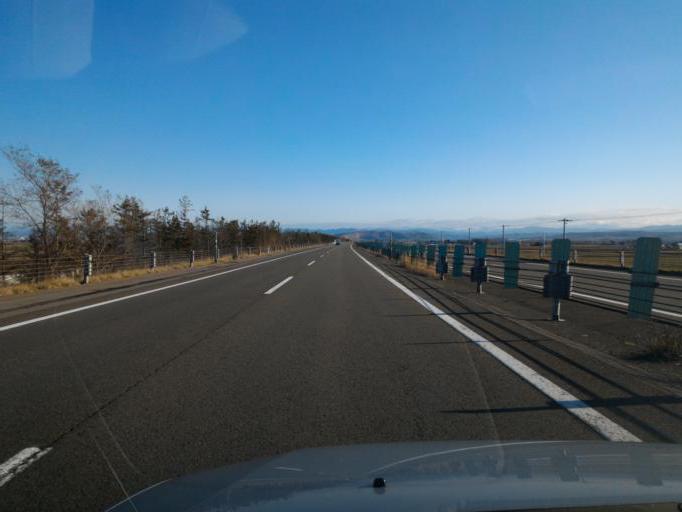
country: JP
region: Hokkaido
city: Iwamizawa
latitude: 43.1509
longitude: 141.7022
